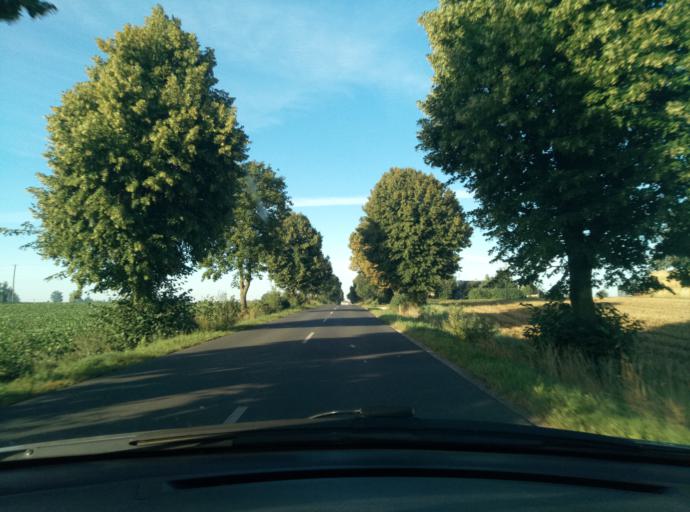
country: PL
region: Kujawsko-Pomorskie
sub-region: Powiat golubsko-dobrzynski
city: Kowalewo Pomorskie
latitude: 53.2084
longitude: 18.9231
